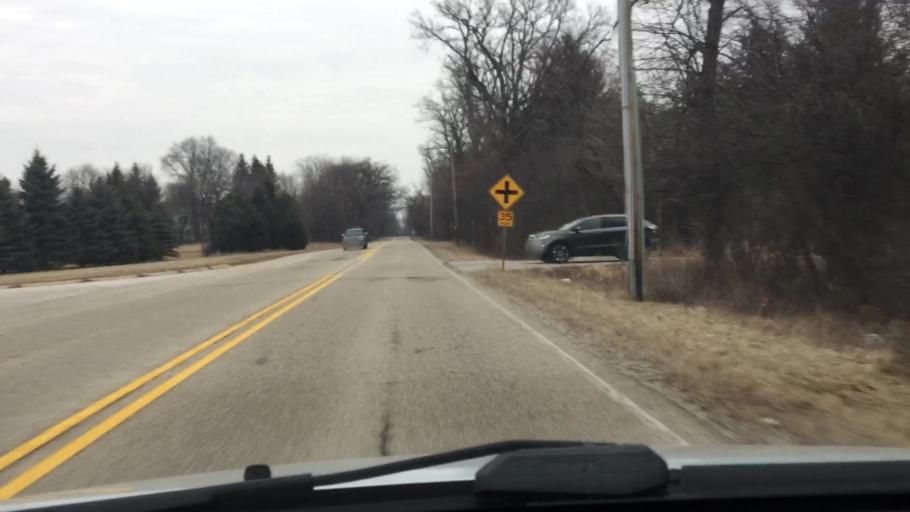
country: US
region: Wisconsin
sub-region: Waukesha County
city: Delafield
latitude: 43.0261
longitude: -88.4040
